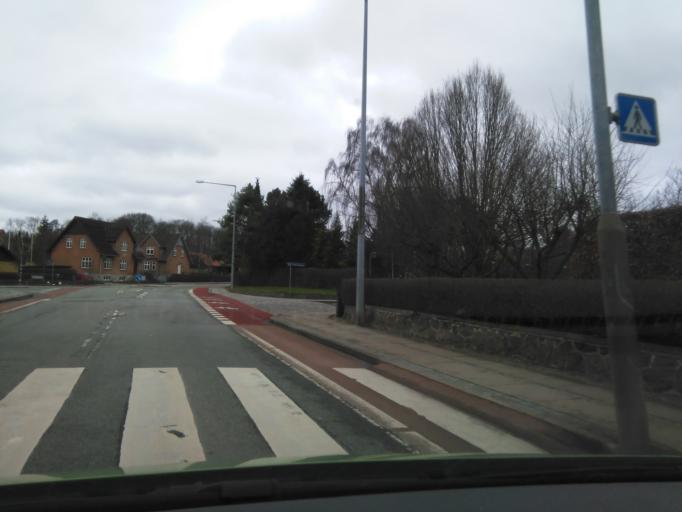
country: DK
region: Central Jutland
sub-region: Odder Kommune
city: Odder
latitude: 55.9718
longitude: 10.1398
